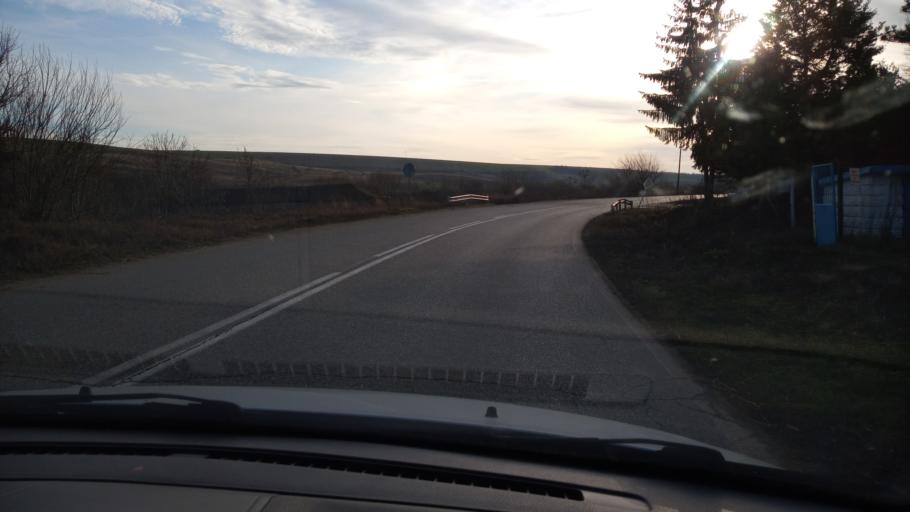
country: BG
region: Pleven
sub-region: Obshtina Pleven
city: Slavyanovo
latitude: 43.5486
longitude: 24.8622
